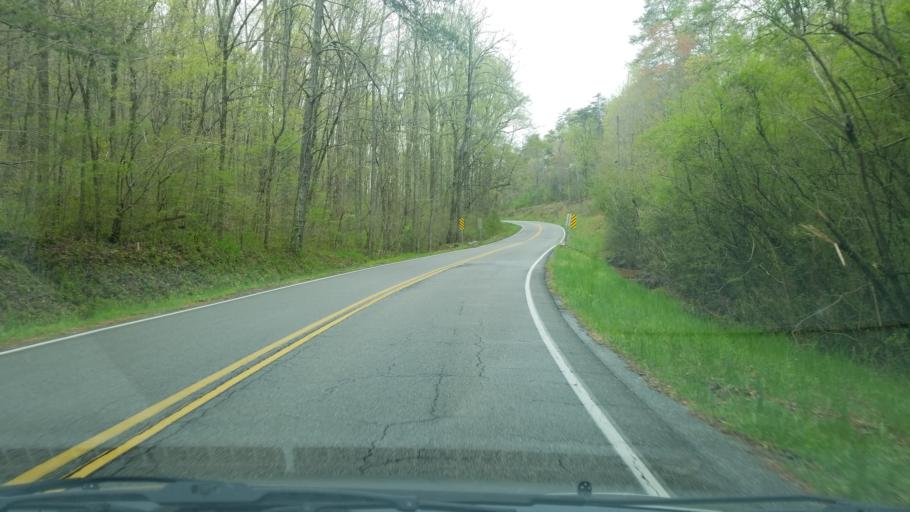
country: US
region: Tennessee
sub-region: Hamilton County
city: Collegedale
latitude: 35.0187
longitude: -85.0717
